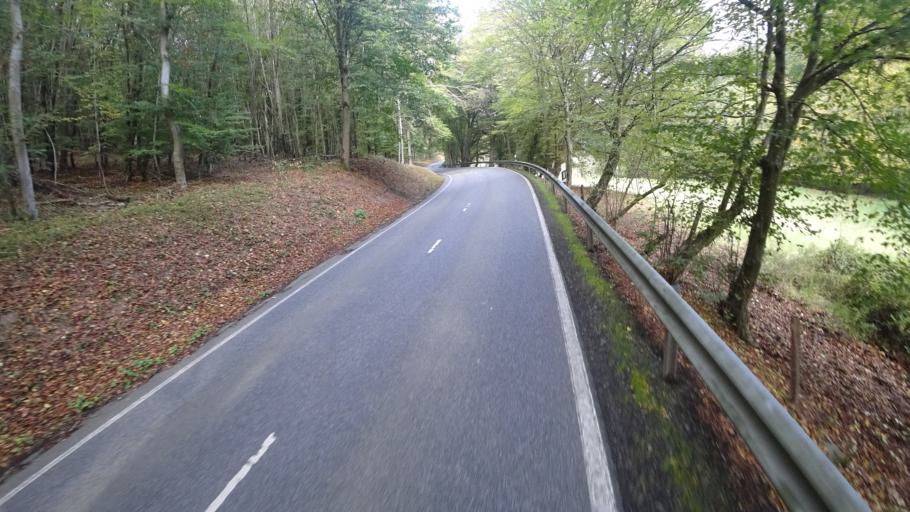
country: DE
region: Rheinland-Pfalz
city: Isselbach
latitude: 50.3913
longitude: 7.9062
